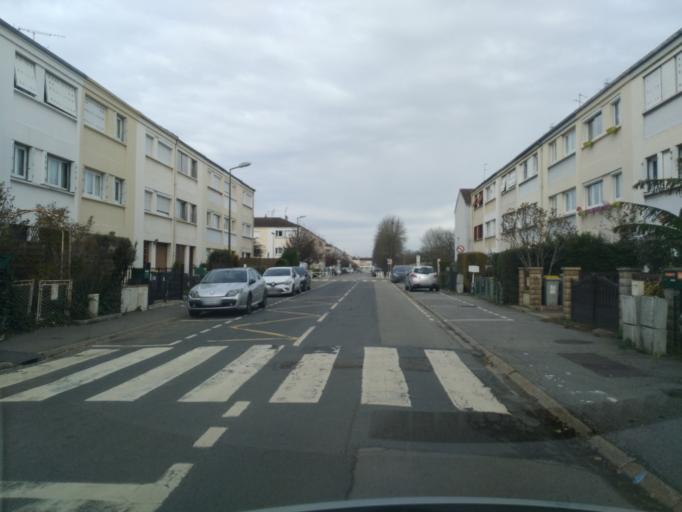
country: FR
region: Ile-de-France
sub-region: Departement des Yvelines
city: Villepreux
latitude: 48.8242
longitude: 1.9997
